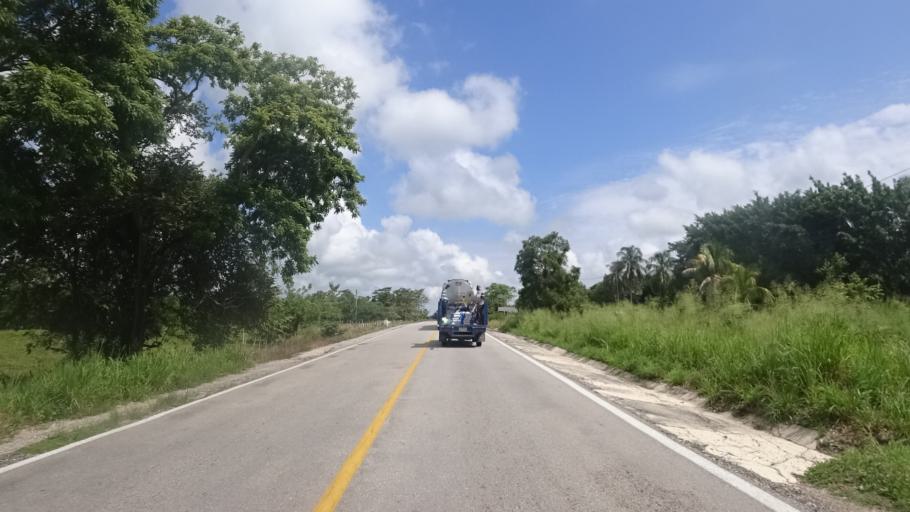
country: MX
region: Chiapas
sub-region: Catazaja
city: Catazaja
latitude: 17.6335
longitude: -92.0283
